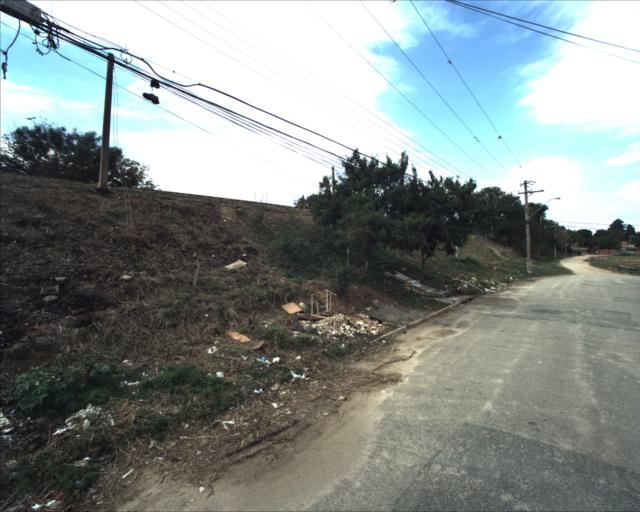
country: BR
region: Sao Paulo
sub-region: Sorocaba
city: Sorocaba
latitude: -23.4972
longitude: -47.4929
